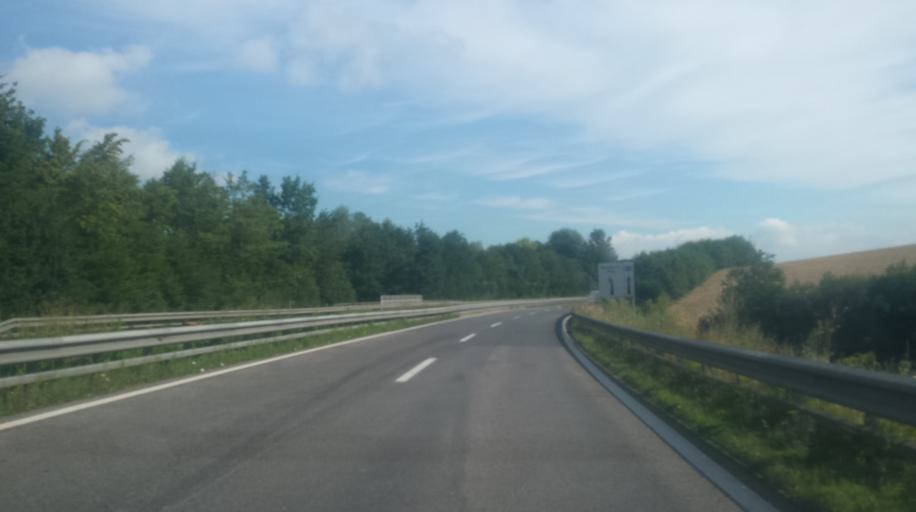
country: AT
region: Upper Austria
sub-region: Politischer Bezirk Grieskirchen
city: Bad Schallerbach
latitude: 48.1932
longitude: 13.9261
